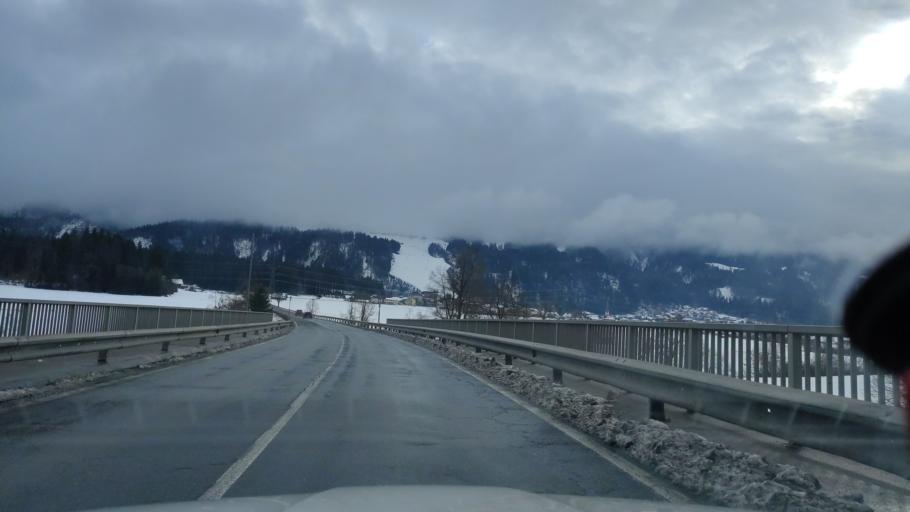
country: AT
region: Carinthia
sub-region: Politischer Bezirk Hermagor
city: Hermagor
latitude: 46.6233
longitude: 13.2879
